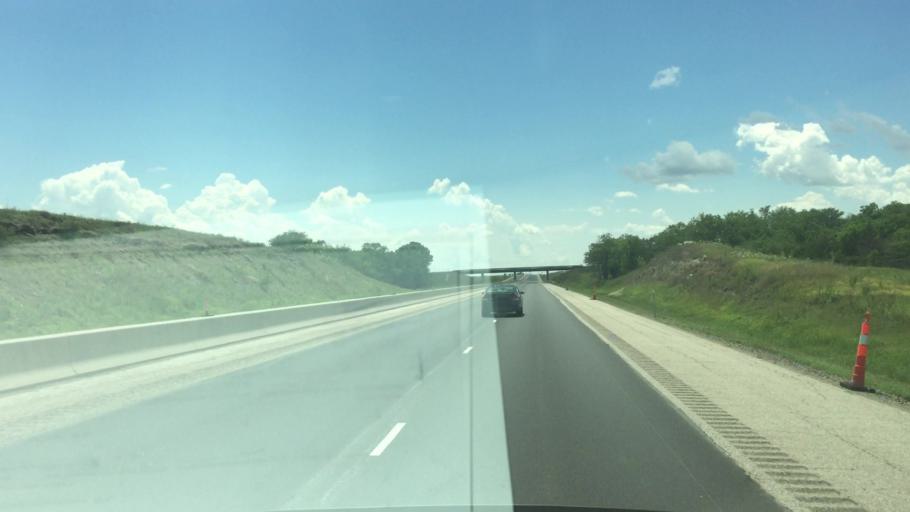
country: US
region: Kansas
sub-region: Osage County
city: Osage City
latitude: 38.7281
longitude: -95.9629
